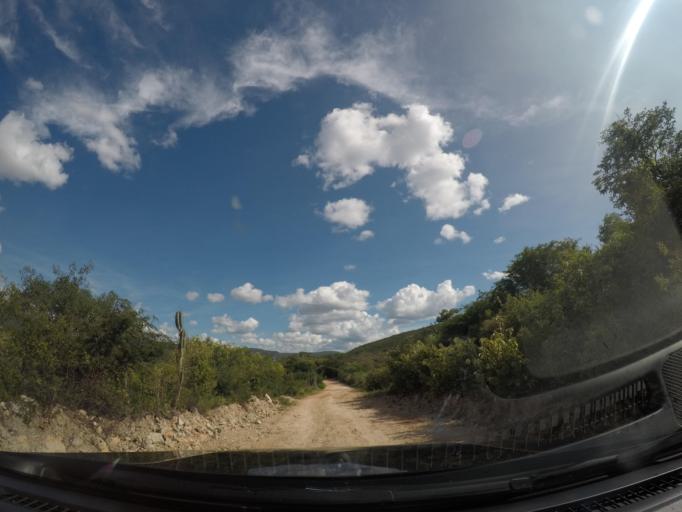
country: BR
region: Bahia
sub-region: Barra Da Estiva
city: Barra da Estiva
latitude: -13.1949
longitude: -41.5973
